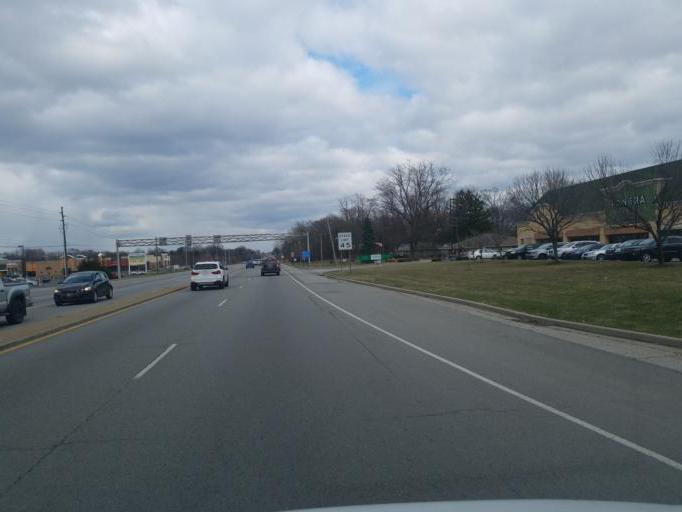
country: US
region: Indiana
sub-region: Marion County
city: Clermont
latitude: 39.7636
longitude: -86.3265
